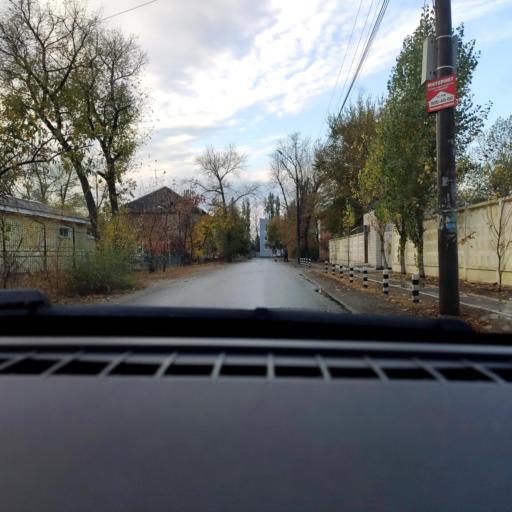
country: RU
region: Voronezj
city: Voronezh
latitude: 51.6641
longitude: 39.2756
